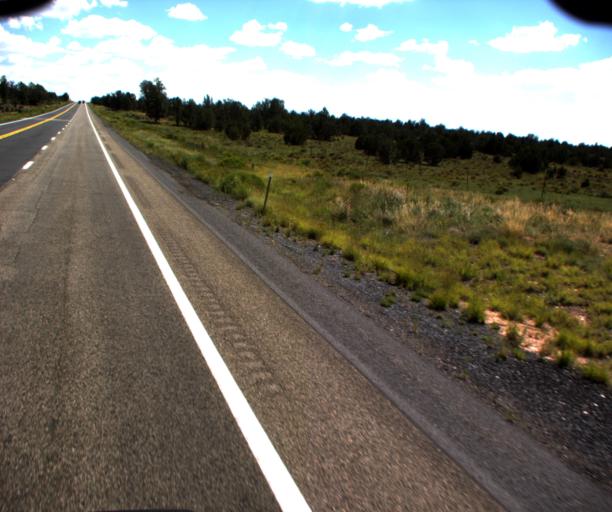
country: US
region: Arizona
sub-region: Coconino County
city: Grand Canyon Village
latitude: 35.8290
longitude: -112.1320
